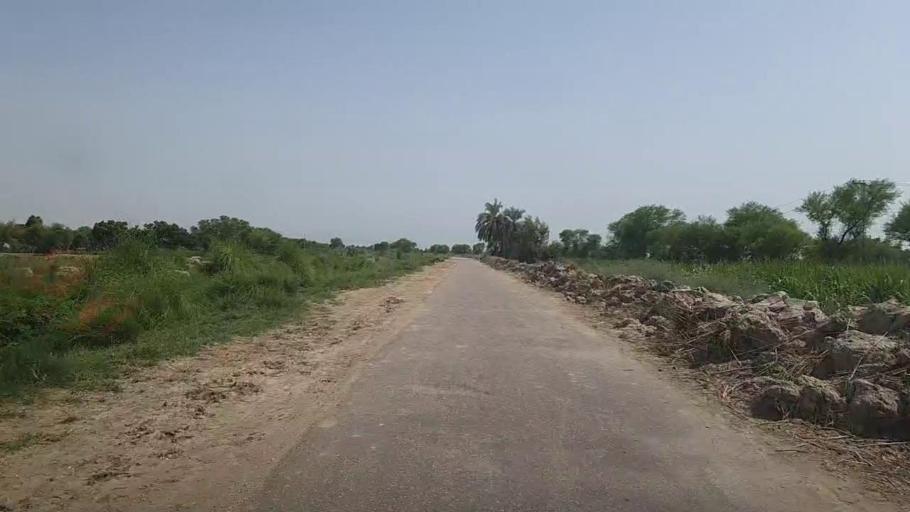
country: PK
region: Sindh
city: Pad Idan
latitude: 26.8164
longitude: 68.3277
